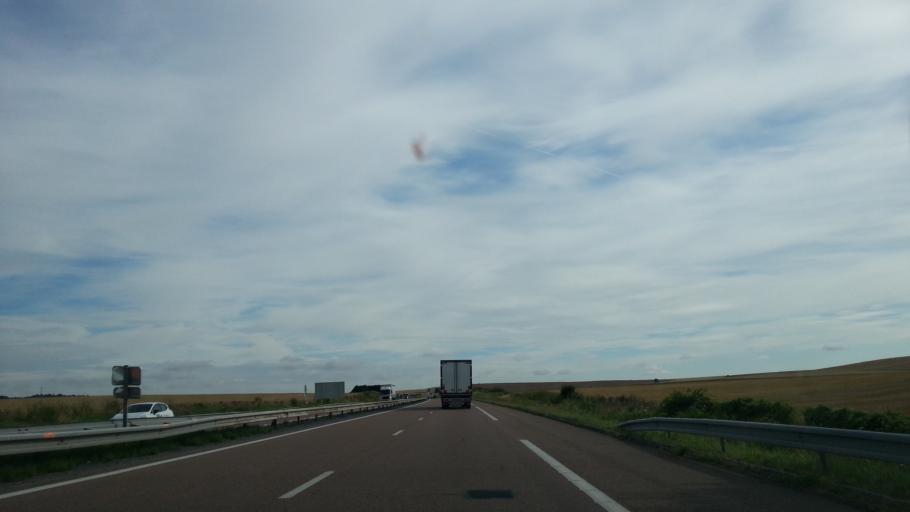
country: FR
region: Champagne-Ardenne
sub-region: Departement de la Marne
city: Chatillon-sur-Marne
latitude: 49.1716
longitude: 3.7430
